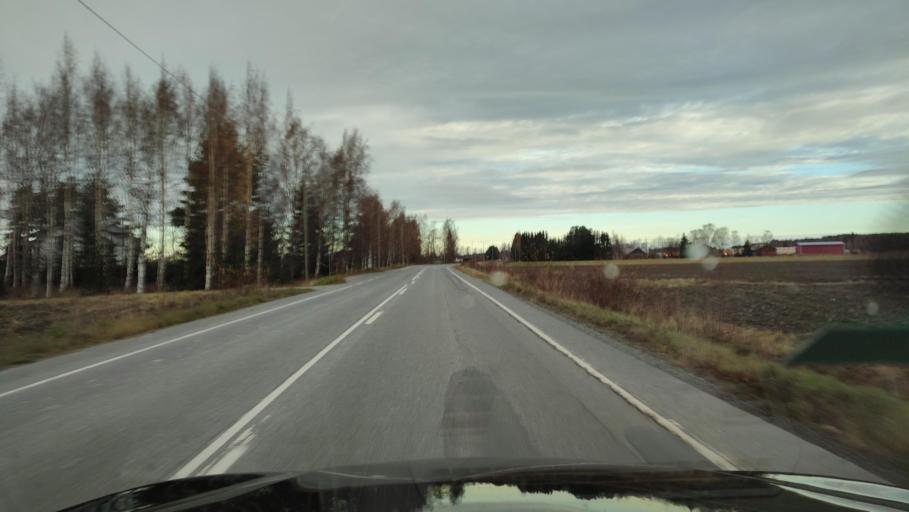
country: FI
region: Ostrobothnia
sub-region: Sydosterbotten
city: Naerpes
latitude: 62.4518
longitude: 21.3531
